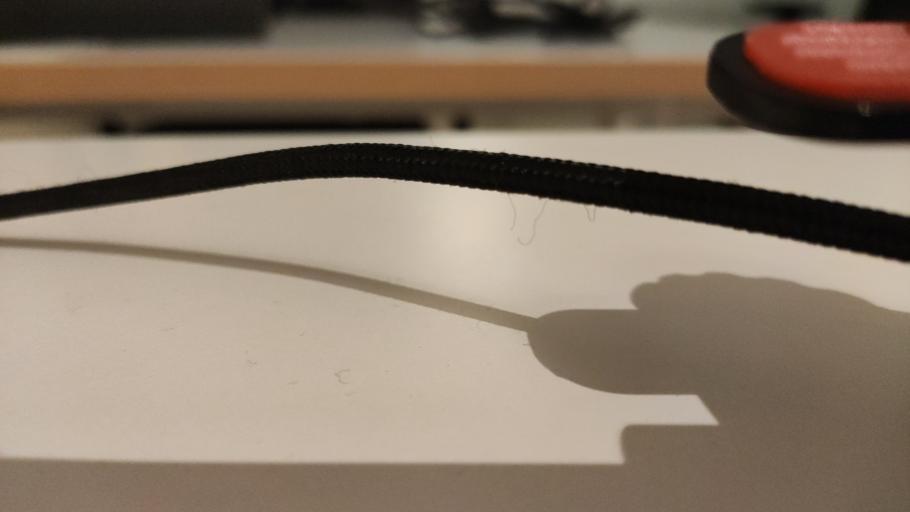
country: RU
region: Moskovskaya
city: Il'inskiy Pogost
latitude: 55.5307
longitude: 38.8724
